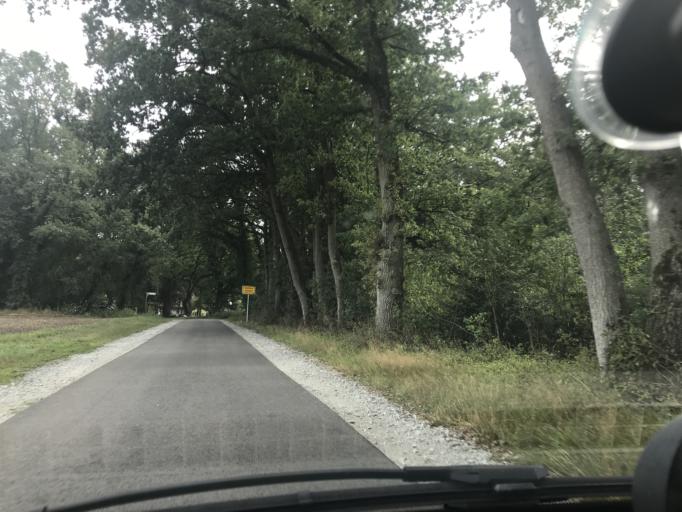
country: DE
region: Lower Saxony
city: Hollenstedt
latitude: 53.3875
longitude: 9.7264
